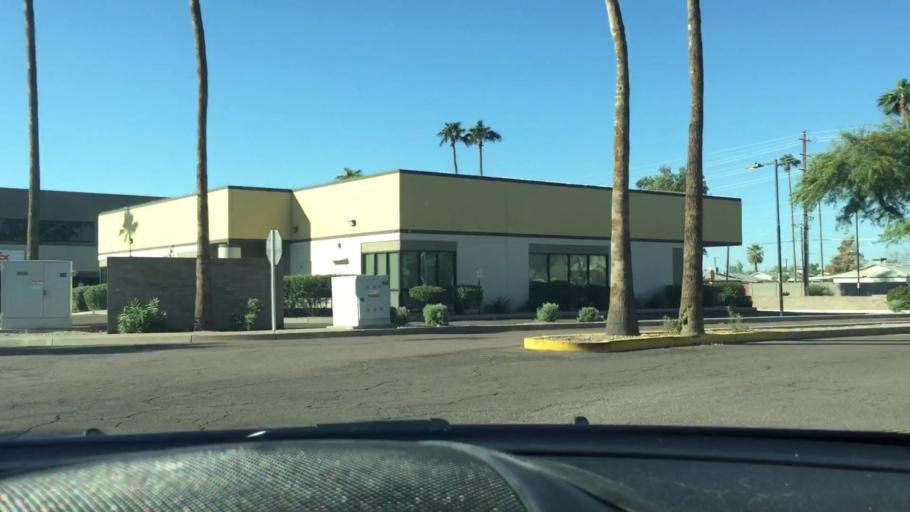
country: US
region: Arizona
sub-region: Maricopa County
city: Scottsdale
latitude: 33.4641
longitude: -111.9081
